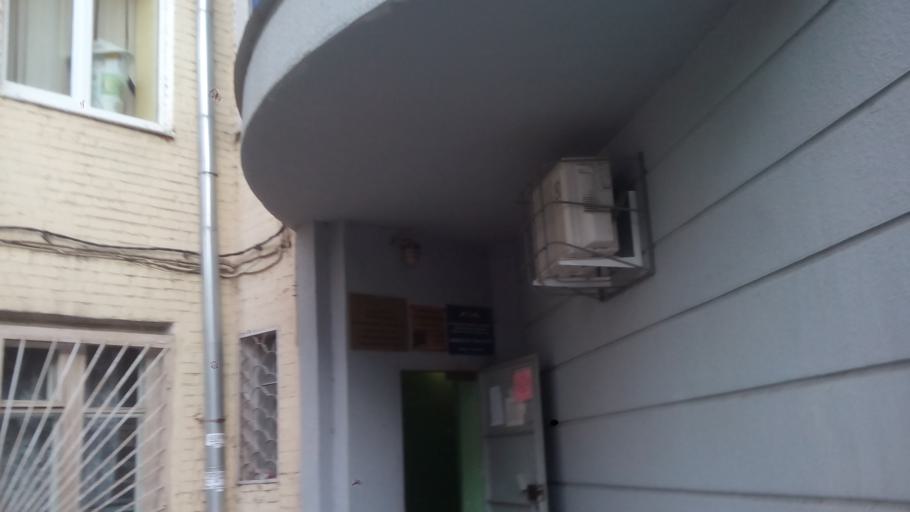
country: RU
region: Rostov
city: Imeni Chkalova
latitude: 47.2515
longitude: 39.7693
